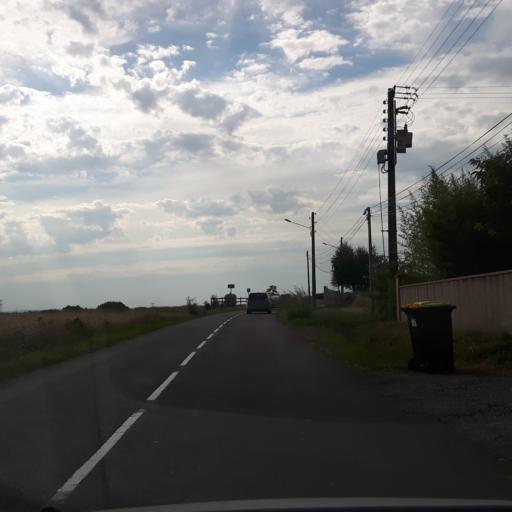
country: FR
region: Midi-Pyrenees
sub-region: Departement de la Haute-Garonne
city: Castelnau-d'Estretefonds
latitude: 43.7737
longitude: 1.3761
